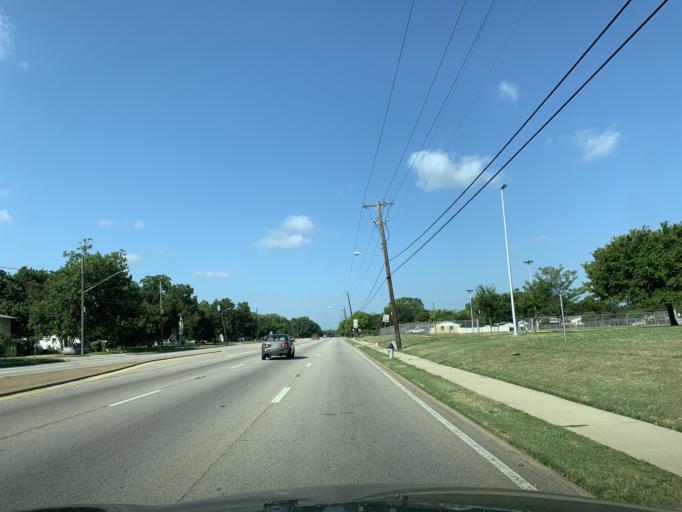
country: US
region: Texas
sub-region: Dallas County
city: Hutchins
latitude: 32.6902
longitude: -96.7815
